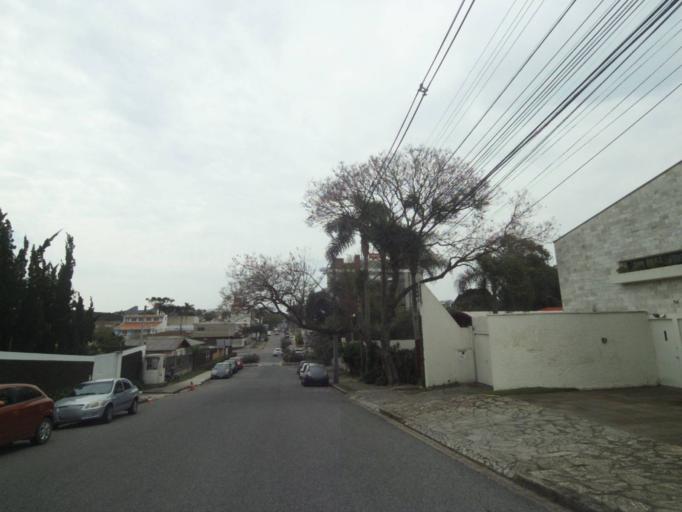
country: BR
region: Parana
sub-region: Curitiba
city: Curitiba
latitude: -25.4538
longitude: -49.3059
